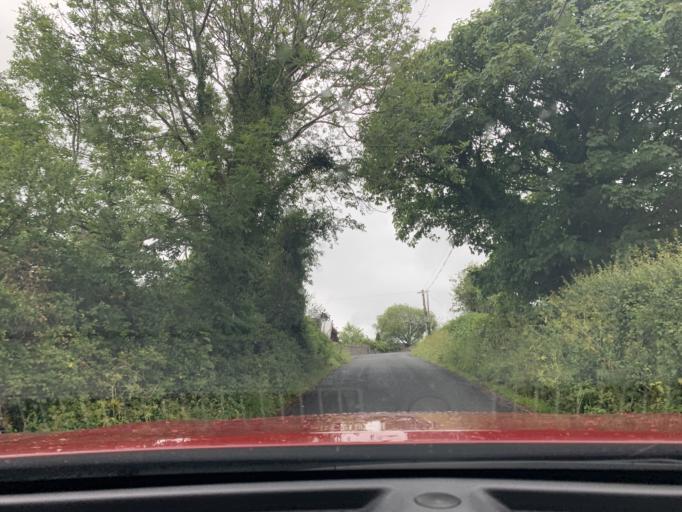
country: IE
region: Connaught
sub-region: Sligo
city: Sligo
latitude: 54.3047
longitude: -8.4563
